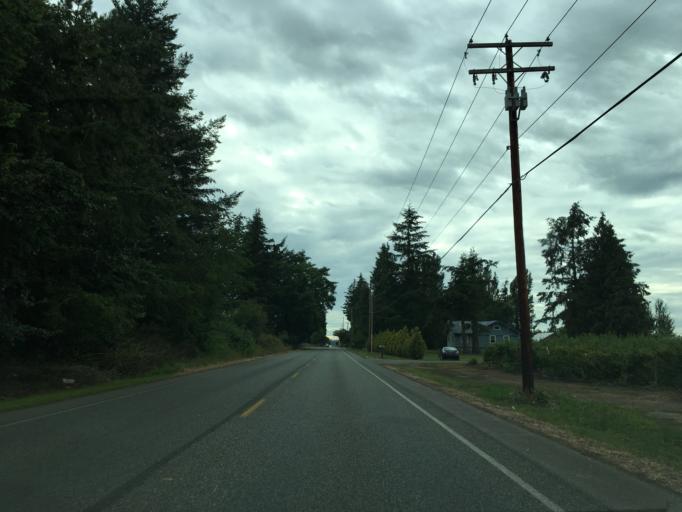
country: US
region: Washington
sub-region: Whatcom County
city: Lynden
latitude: 48.8879
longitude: -122.5136
